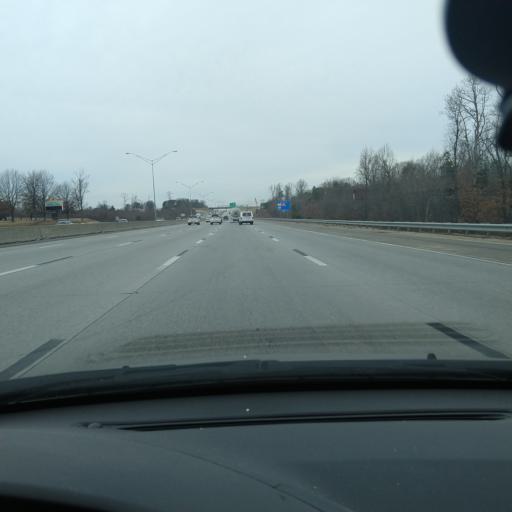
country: US
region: North Carolina
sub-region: Guilford County
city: Oak Ridge
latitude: 36.0892
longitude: -79.9864
